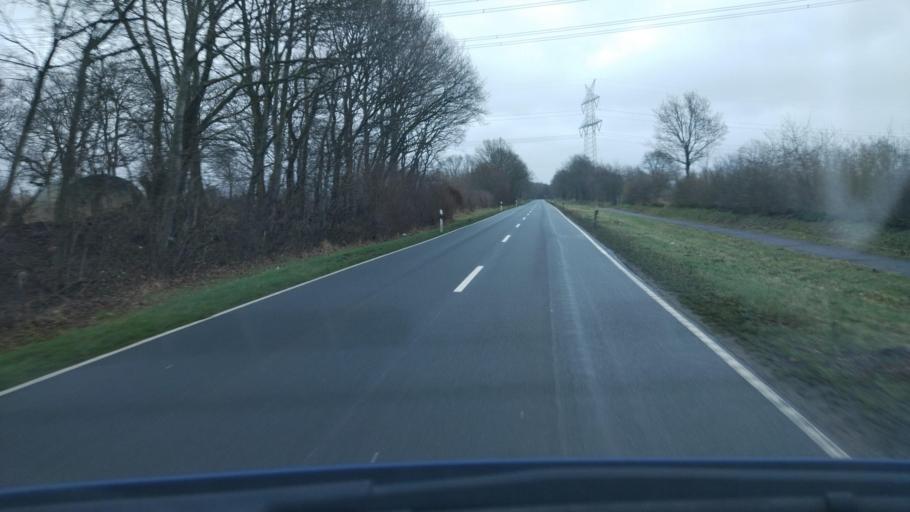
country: DE
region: Schleswig-Holstein
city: Gross Rheide
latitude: 54.4459
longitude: 9.4195
